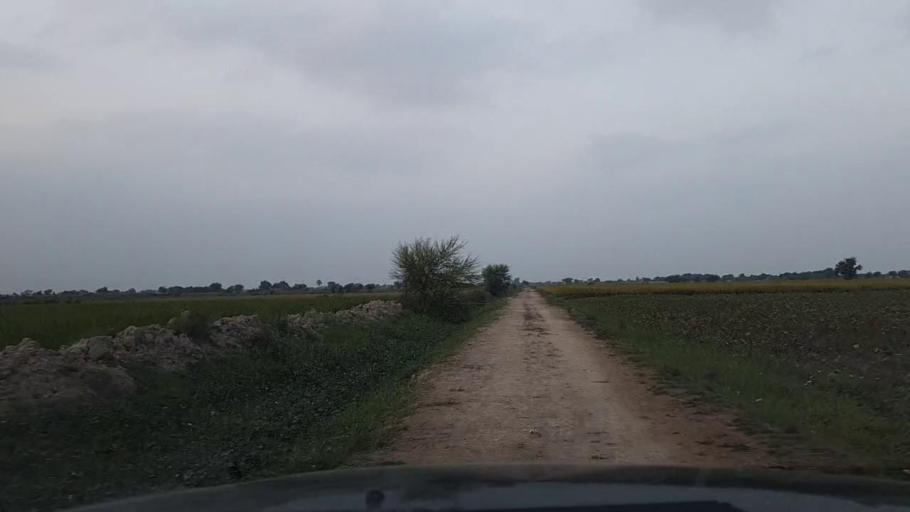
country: PK
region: Sindh
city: Jati
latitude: 24.5058
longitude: 68.3931
